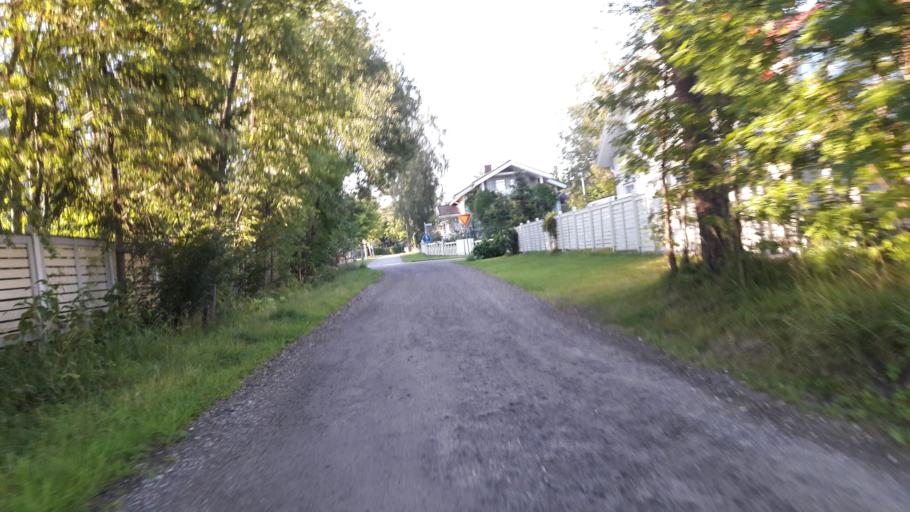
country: FI
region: North Karelia
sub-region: Joensuu
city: Joensuu
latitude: 62.6138
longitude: 29.7077
